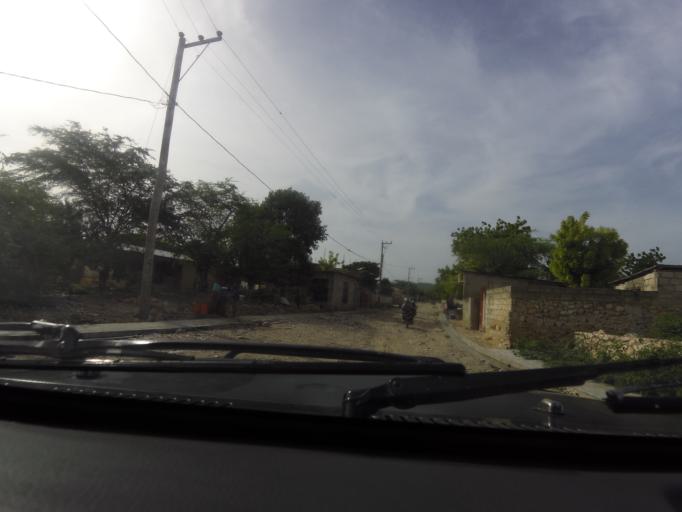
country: HT
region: Ouest
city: Anse a Galets
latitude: 18.8369
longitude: -72.8635
